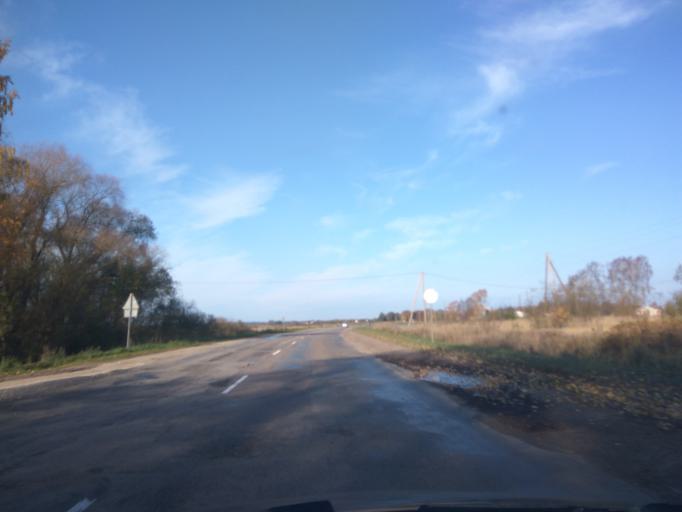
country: LV
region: Ventspils
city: Ventspils
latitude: 57.3082
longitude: 21.5568
